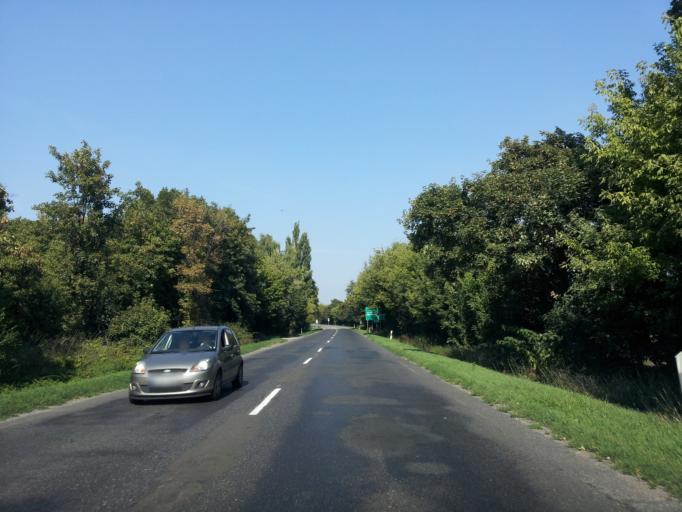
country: HU
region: Fejer
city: Lepseny
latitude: 46.9676
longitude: 18.2011
